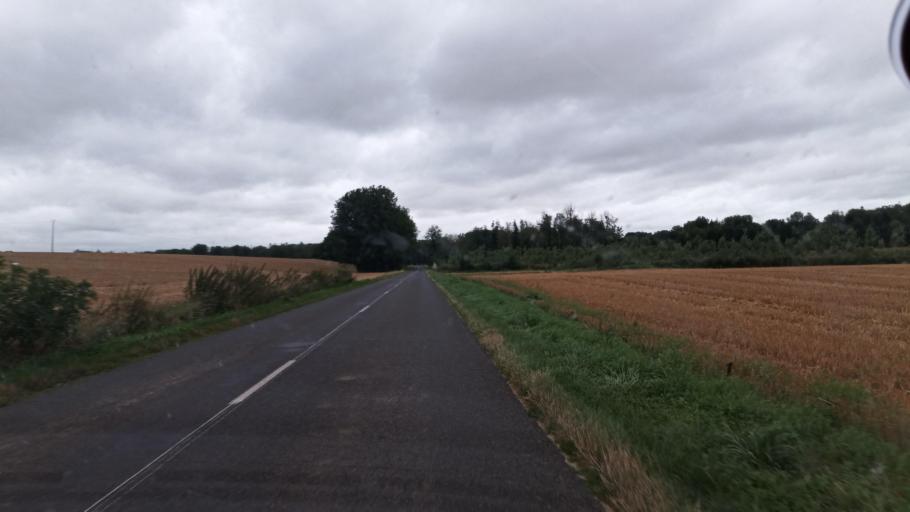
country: FR
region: Ile-de-France
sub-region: Departement de Seine-et-Marne
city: Voulx
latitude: 48.2731
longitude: 2.9968
